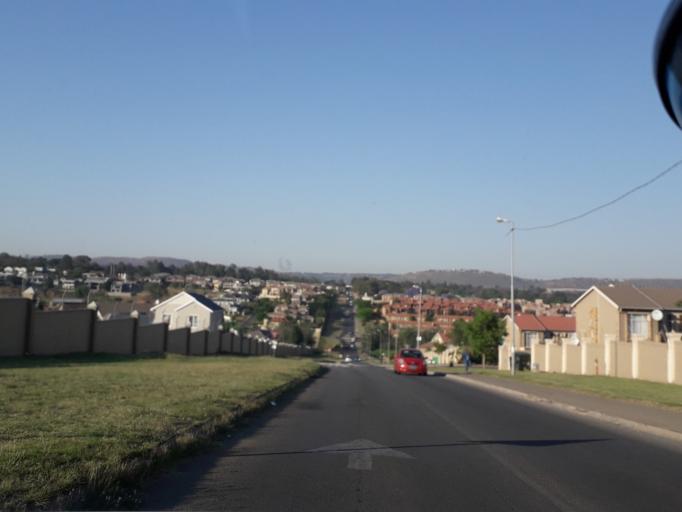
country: ZA
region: Gauteng
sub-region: West Rand District Municipality
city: Muldersdriseloop
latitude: -26.0833
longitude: 27.9102
